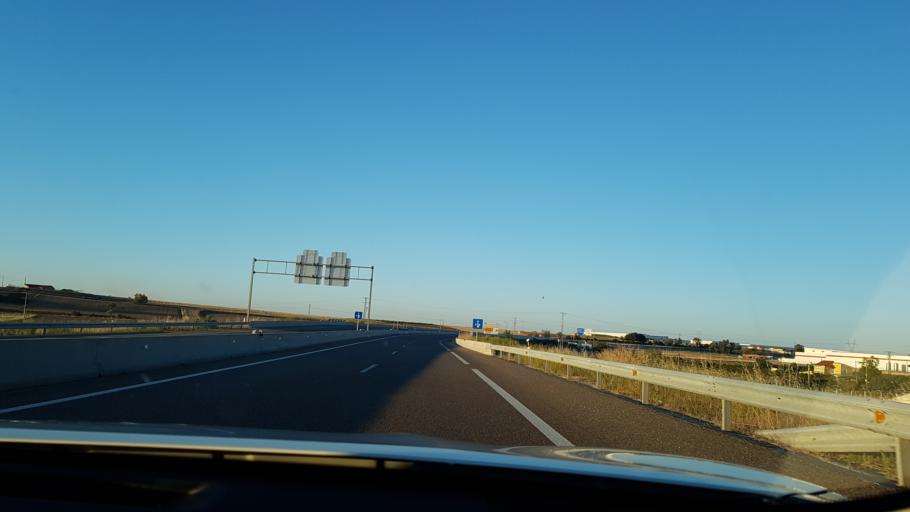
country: ES
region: Castille and Leon
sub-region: Provincia de Zamora
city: Valcabado
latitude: 41.5486
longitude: -5.7576
